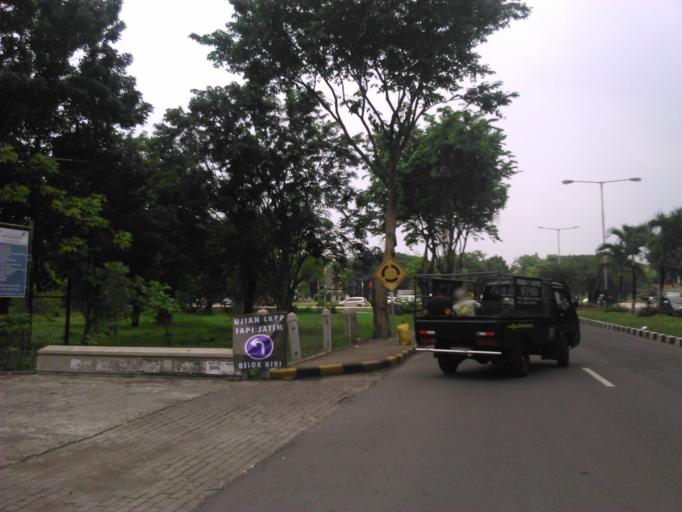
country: ID
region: East Java
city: Mulyorejo
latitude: -7.2781
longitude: 112.7903
